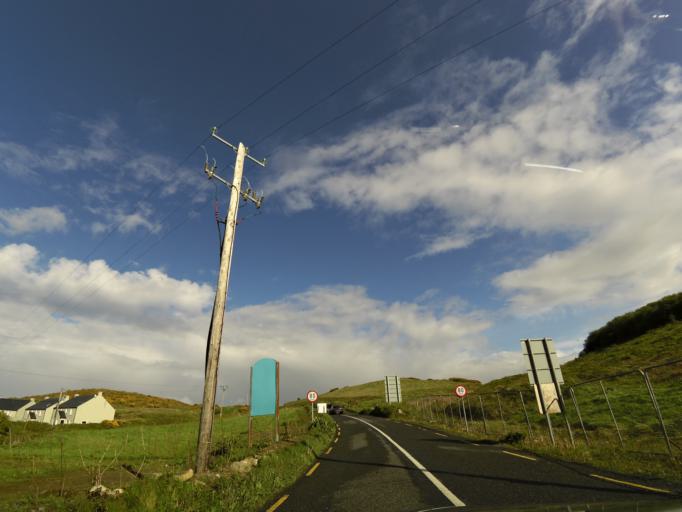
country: IE
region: Connaught
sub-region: County Galway
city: Bearna
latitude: 53.0155
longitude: -9.3763
